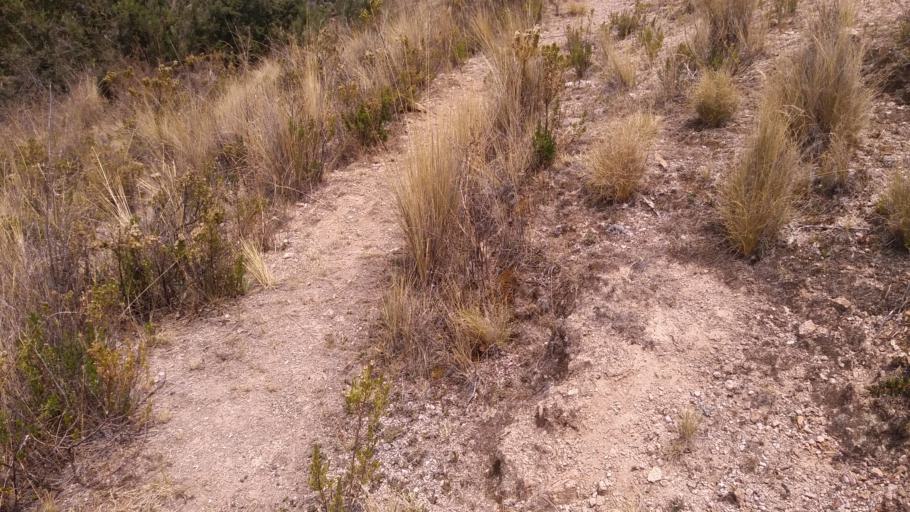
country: PE
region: Puno
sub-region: Yunguyo
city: Yunguyo
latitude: -16.1847
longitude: -69.0838
